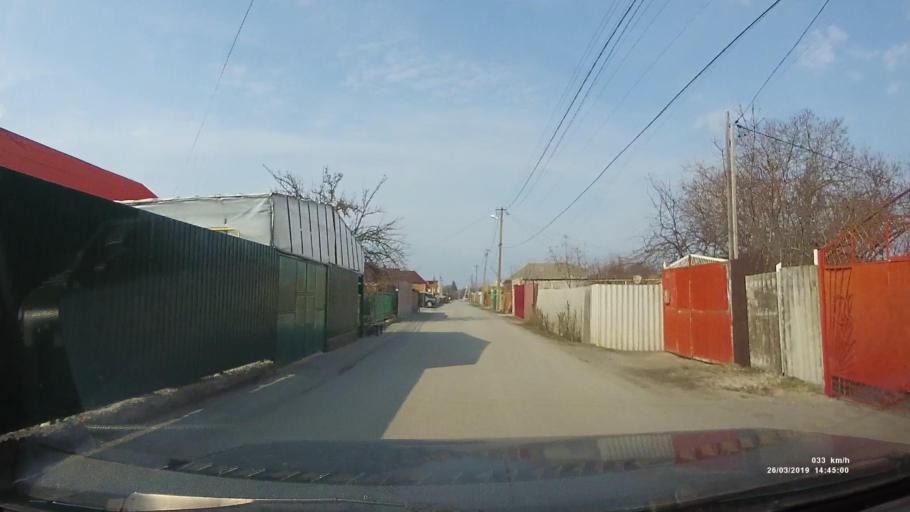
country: RU
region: Rostov
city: Novobessergenovka
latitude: 47.1803
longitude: 38.8624
